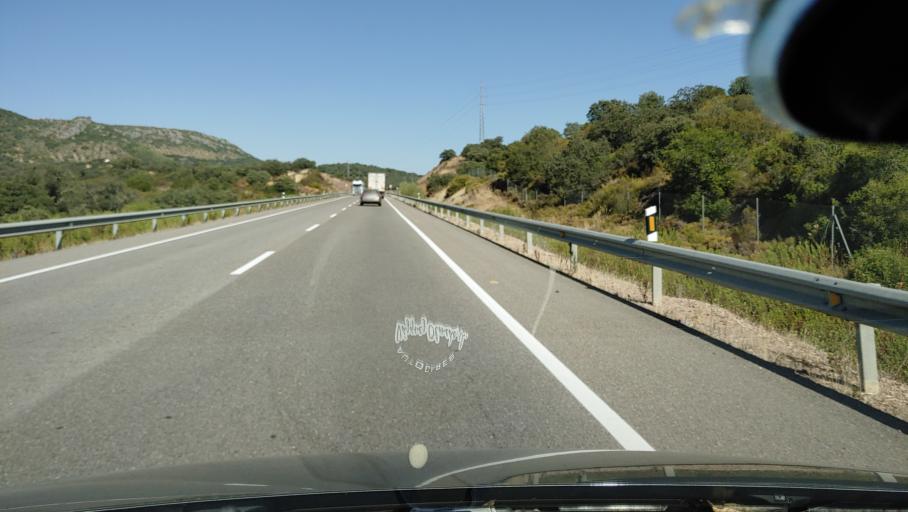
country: ES
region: Andalusia
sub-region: Province of Cordoba
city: Espiel
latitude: 38.1548
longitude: -4.9819
